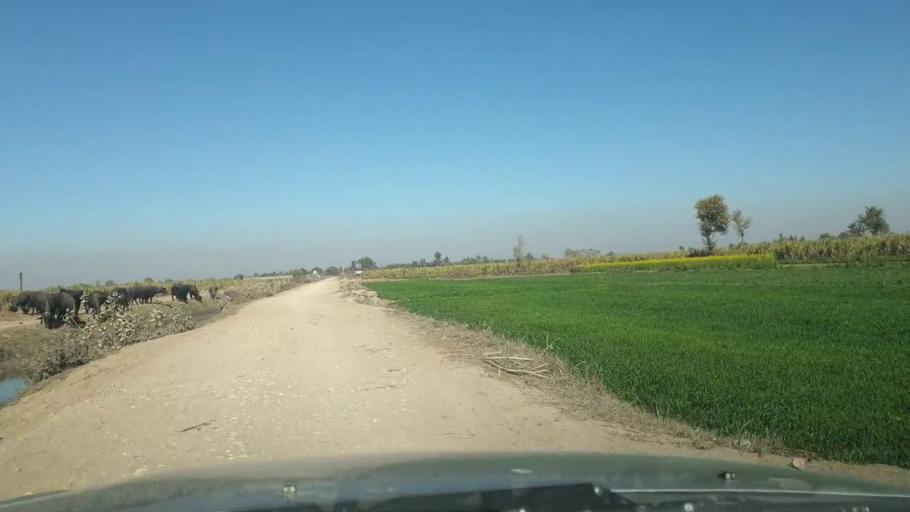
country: PK
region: Sindh
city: Ghotki
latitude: 28.0359
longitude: 69.2465
